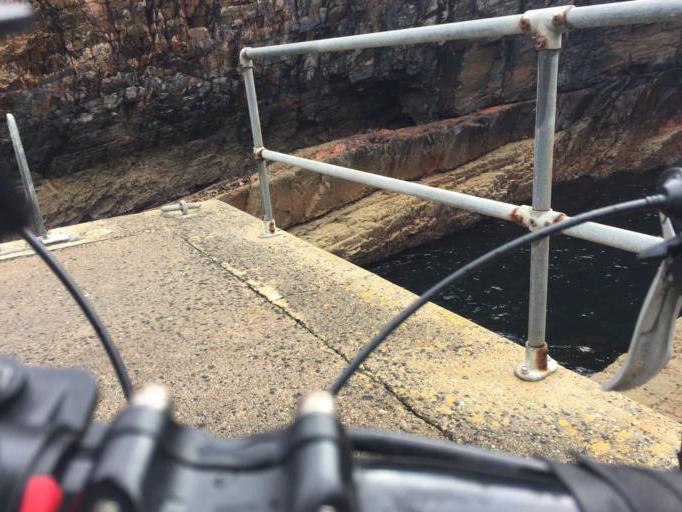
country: IE
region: Ulster
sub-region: County Donegal
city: Derrybeg
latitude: 55.2557
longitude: -8.1945
